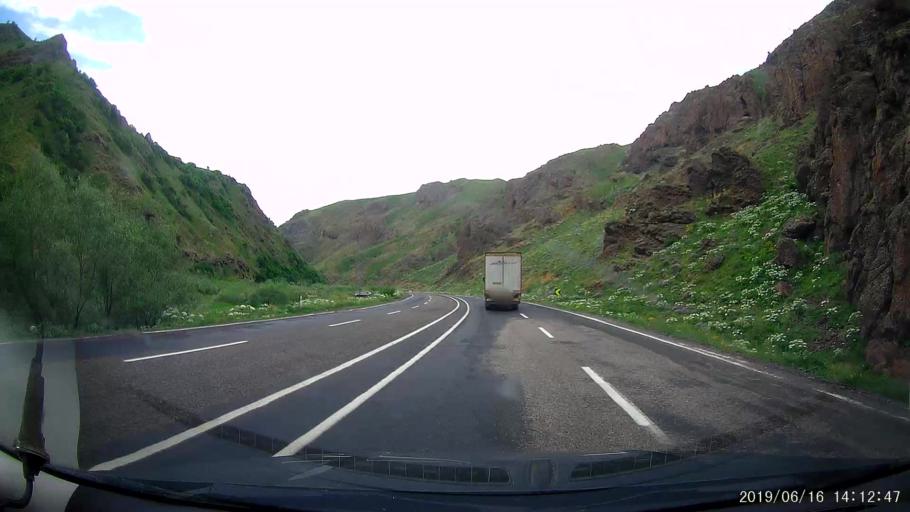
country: TR
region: Agri
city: Tahir
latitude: 39.7990
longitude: 42.5304
